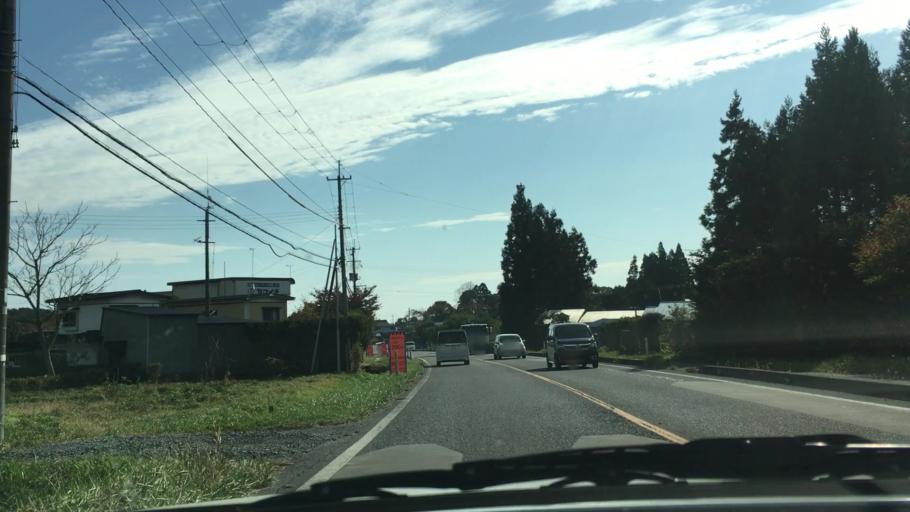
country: JP
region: Aomori
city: Hachinohe
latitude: 40.4274
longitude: 141.6933
